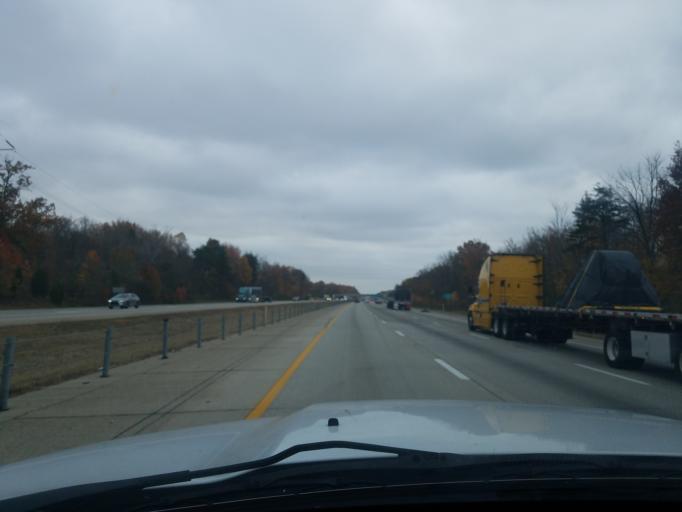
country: US
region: Kentucky
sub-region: Bullitt County
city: Hillview
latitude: 38.0854
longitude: -85.7009
